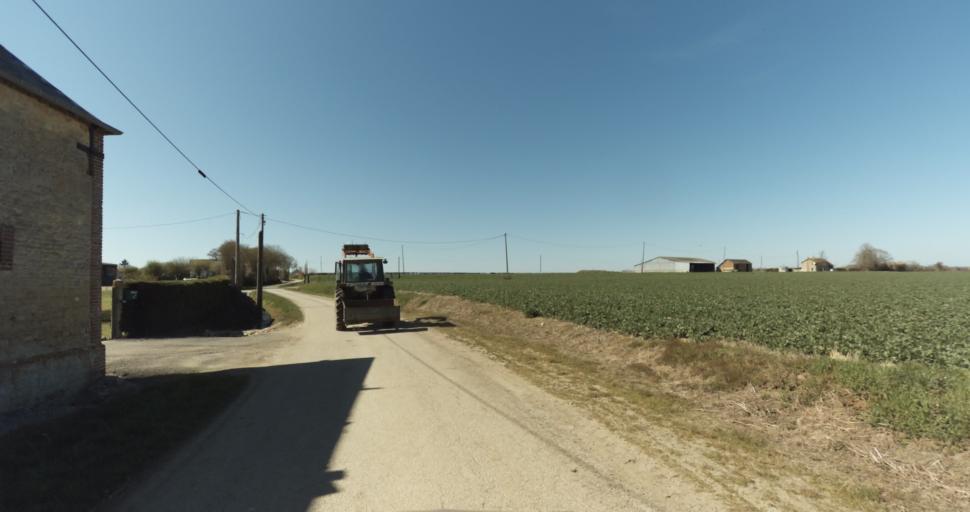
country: FR
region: Lower Normandy
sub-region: Departement du Calvados
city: Saint-Pierre-sur-Dives
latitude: 49.0368
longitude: 0.0032
